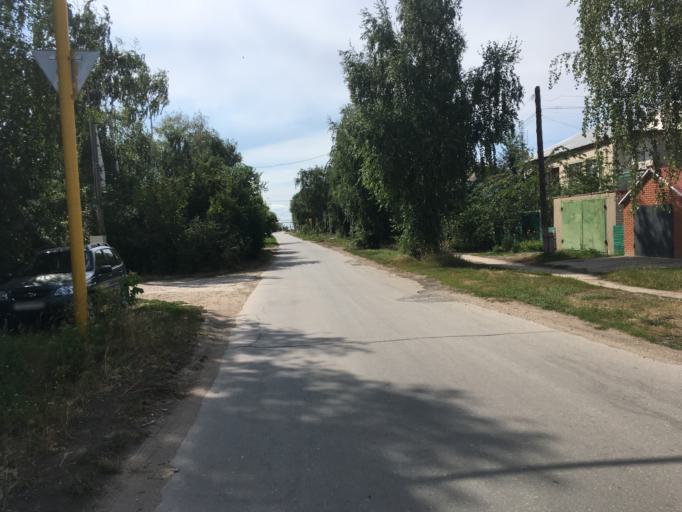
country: RU
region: Samara
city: Bezenchuk
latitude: 52.9881
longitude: 49.4445
